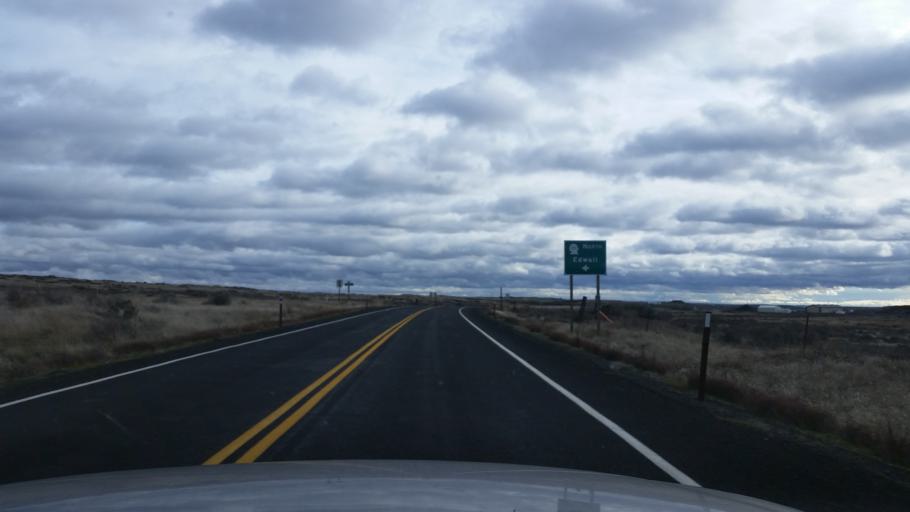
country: US
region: Washington
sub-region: Lincoln County
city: Davenport
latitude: 47.3170
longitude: -117.9752
